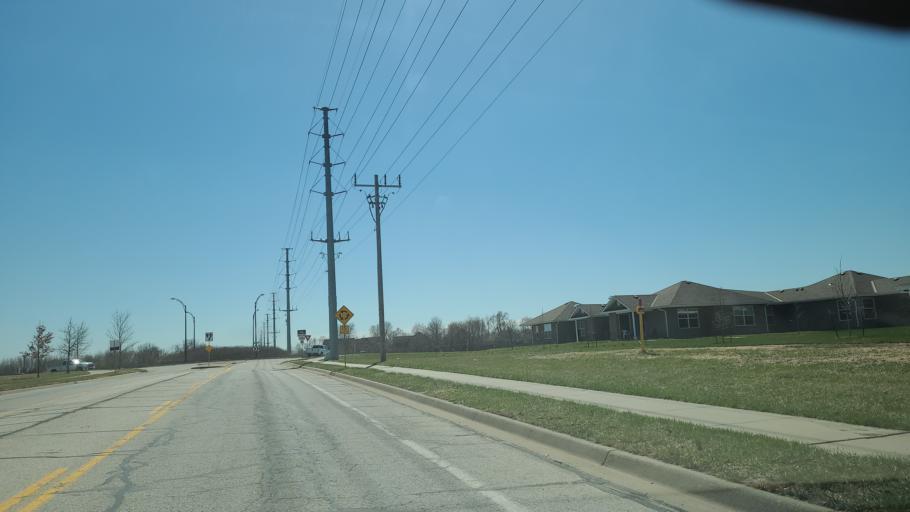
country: US
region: Kansas
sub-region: Douglas County
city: Lawrence
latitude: 38.9403
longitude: -95.2050
